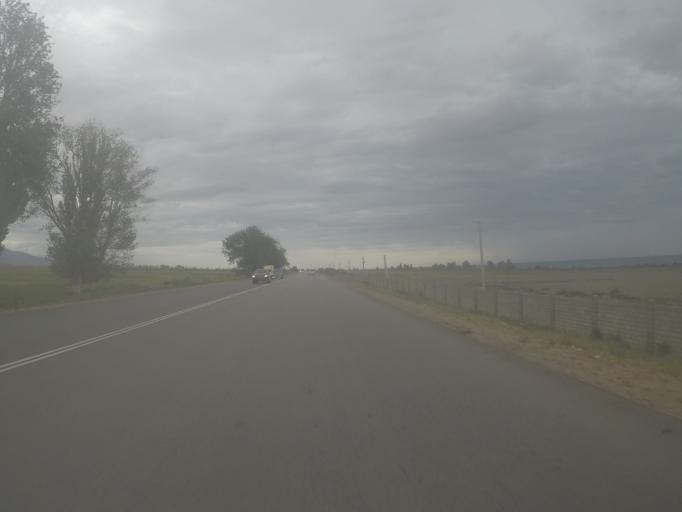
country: KG
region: Ysyk-Koel
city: Cholpon-Ata
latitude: 42.5980
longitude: 76.8033
